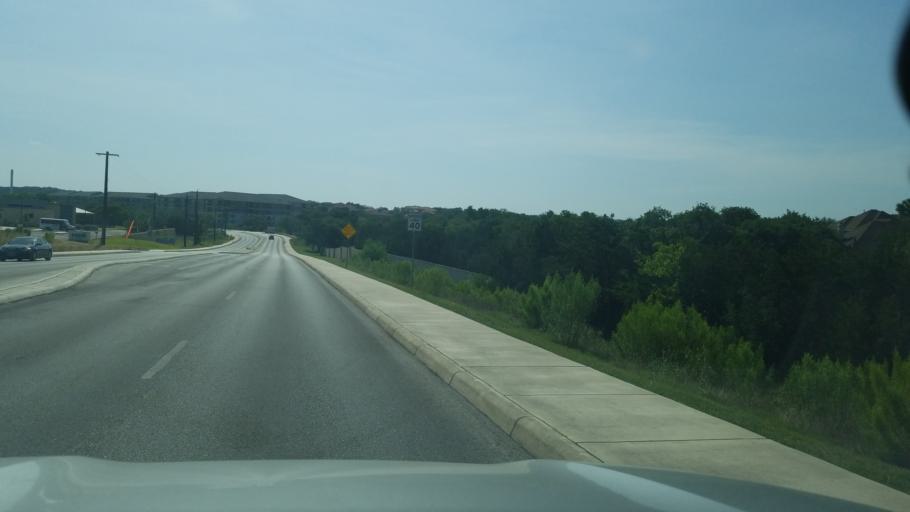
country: US
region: Texas
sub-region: Bexar County
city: Timberwood Park
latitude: 29.6680
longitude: -98.4656
